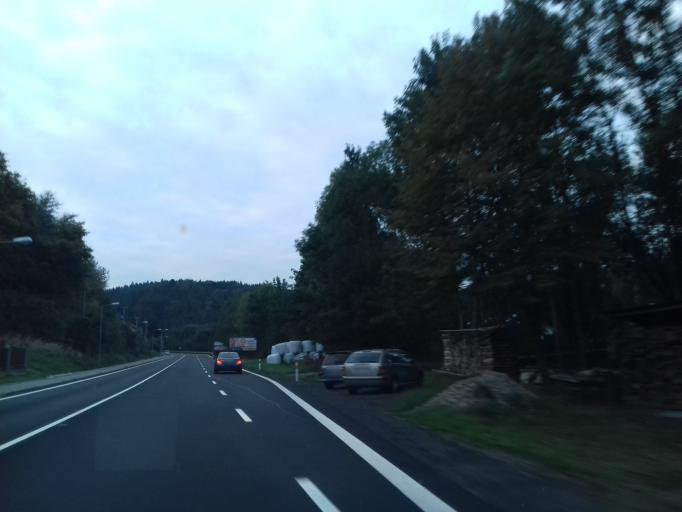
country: CZ
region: Zlin
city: Bojkovice
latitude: 48.9696
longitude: 17.8609
